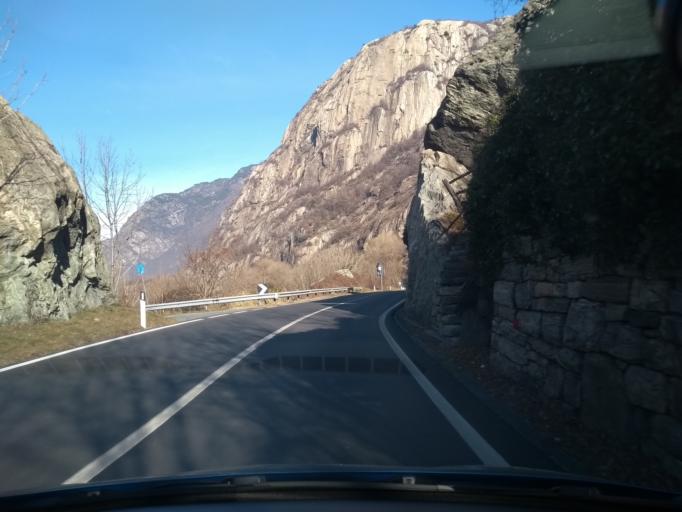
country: IT
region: Aosta Valley
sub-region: Valle d'Aosta
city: Hone
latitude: 45.6264
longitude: 7.7365
